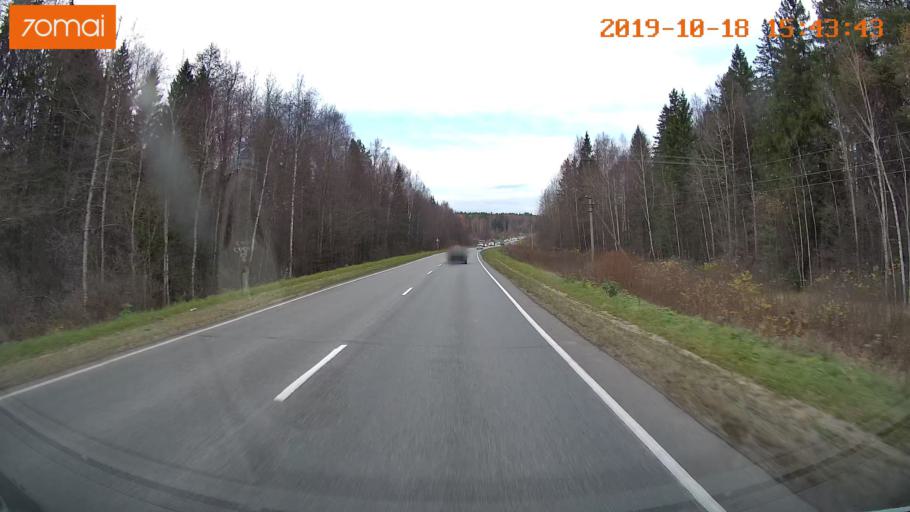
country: RU
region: Vladimir
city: Golovino
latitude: 55.9717
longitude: 40.5482
